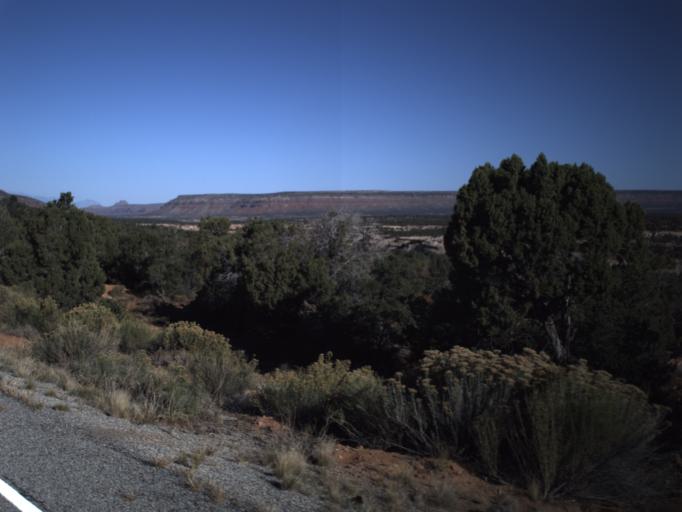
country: US
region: Utah
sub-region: San Juan County
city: Blanding
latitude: 37.5427
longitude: -109.9776
